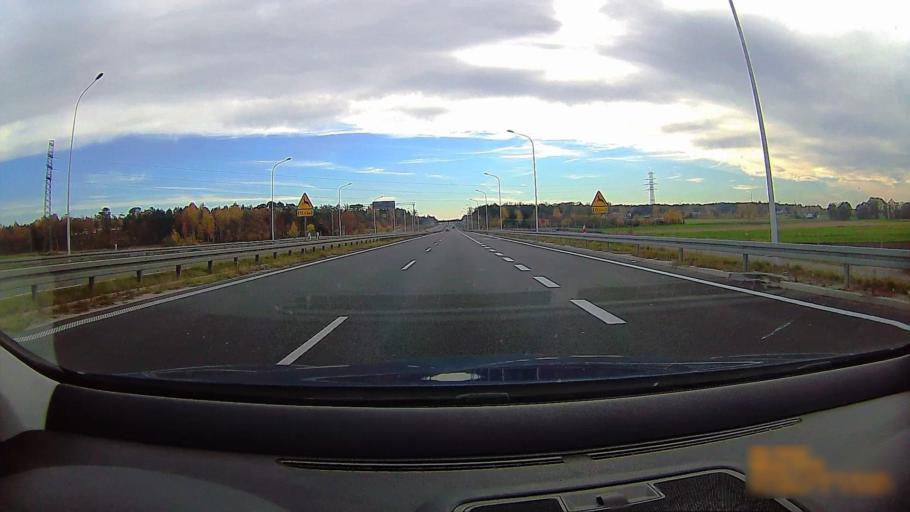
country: PL
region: Greater Poland Voivodeship
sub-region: Powiat ostrowski
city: Ostrow Wielkopolski
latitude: 51.6620
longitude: 17.8590
